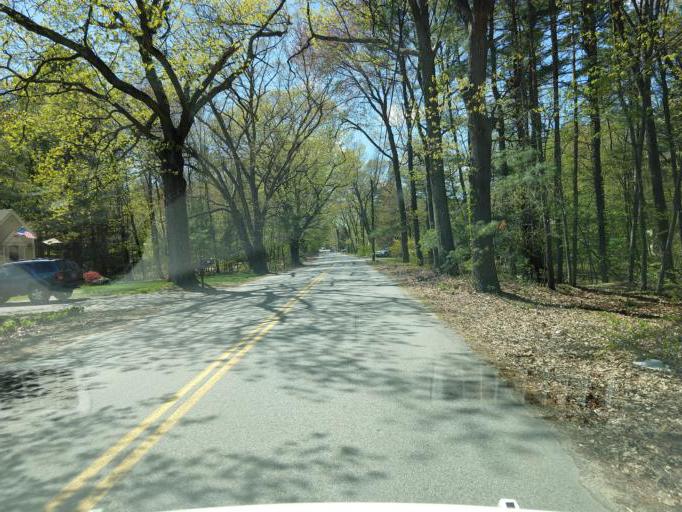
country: US
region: New Hampshire
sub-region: Rockingham County
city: Seabrook
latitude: 42.8828
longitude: -70.8891
